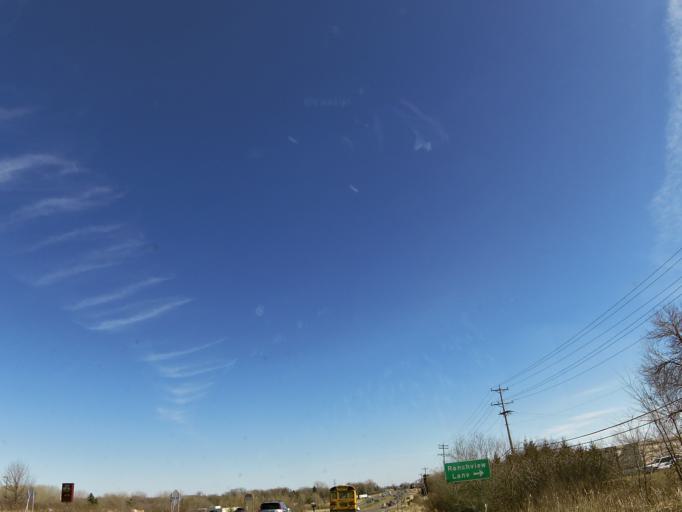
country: US
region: Minnesota
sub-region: Hennepin County
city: Plymouth
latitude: 45.0181
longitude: -93.4788
